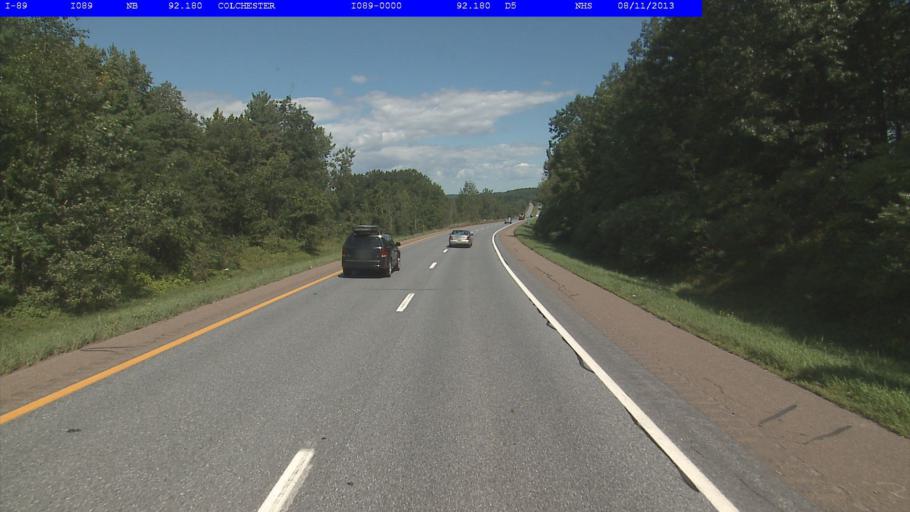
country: US
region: Vermont
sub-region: Chittenden County
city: Winooski
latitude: 44.5122
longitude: -73.1909
